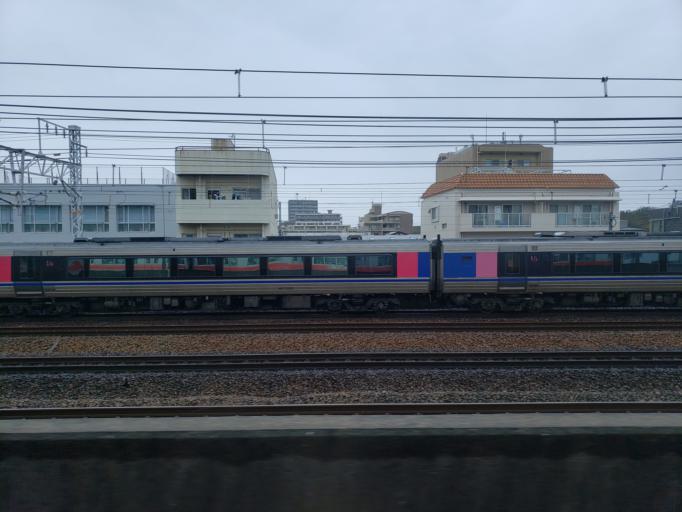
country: JP
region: Hyogo
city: Akashi
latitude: 34.6500
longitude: 134.9873
